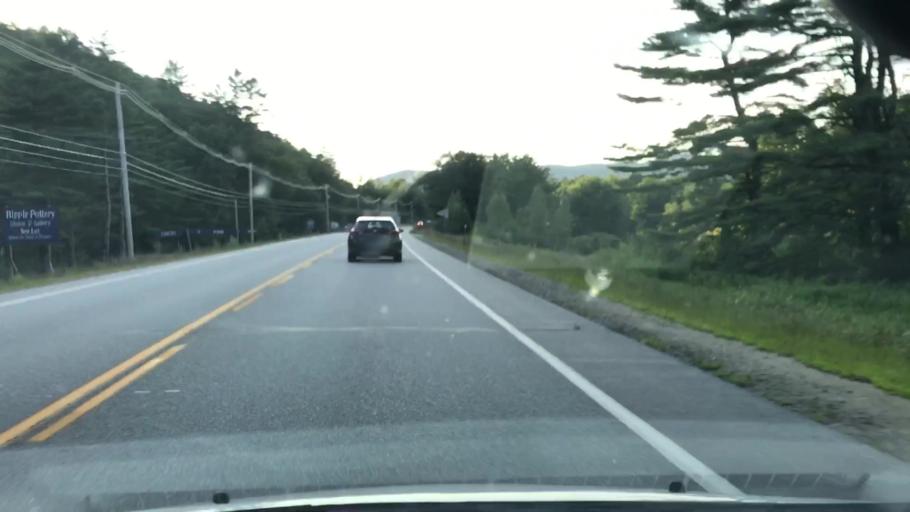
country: US
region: New Hampshire
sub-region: Grafton County
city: Rumney
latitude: 43.7832
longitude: -71.7827
